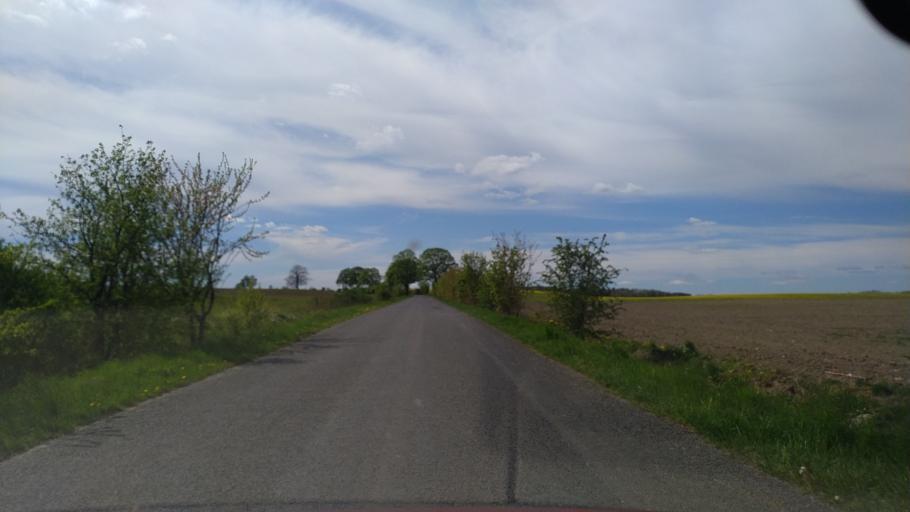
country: PL
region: West Pomeranian Voivodeship
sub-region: Powiat walecki
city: Walcz
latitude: 53.3537
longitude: 16.3255
